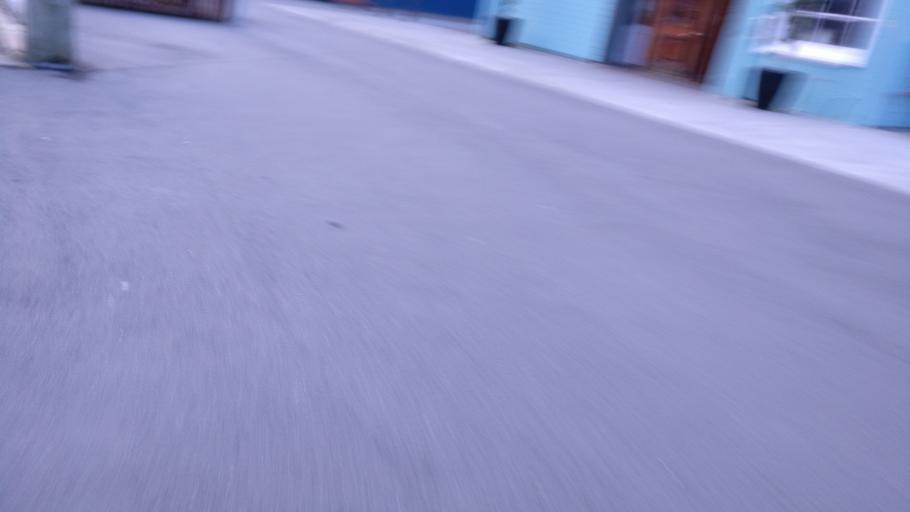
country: NZ
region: Wellington
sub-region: Wellington City
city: Wellington
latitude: -41.2848
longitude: 174.7792
